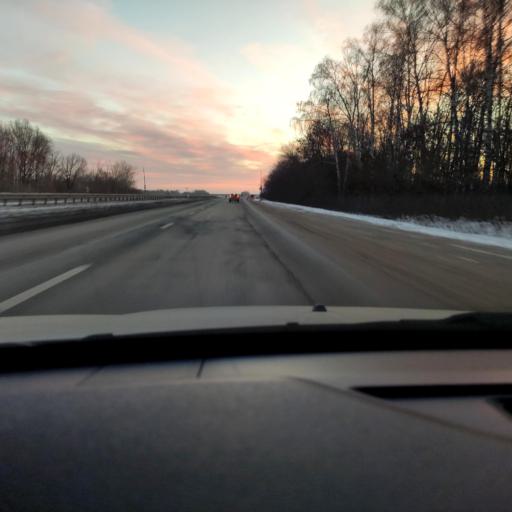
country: RU
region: Samara
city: Smyshlyayevka
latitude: 53.2600
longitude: 50.4629
